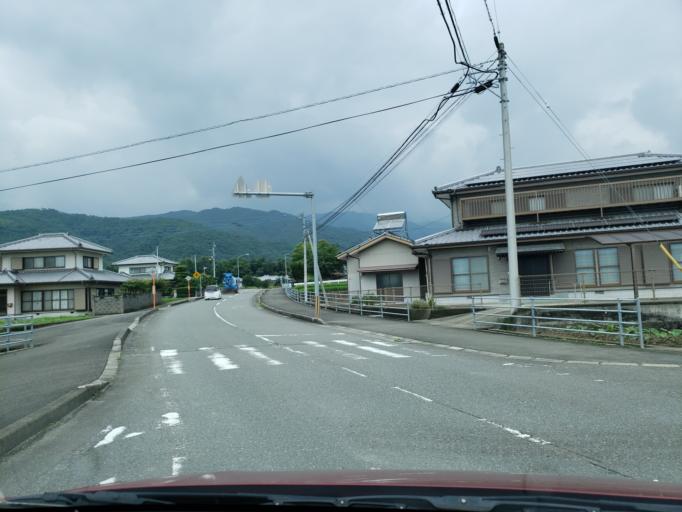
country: JP
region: Tokushima
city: Wakimachi
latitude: 34.0963
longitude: 134.2278
